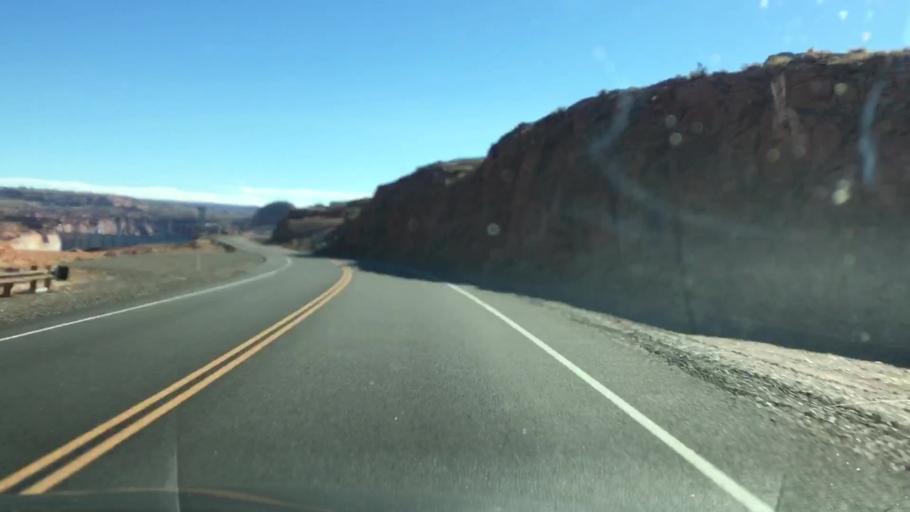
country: US
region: Arizona
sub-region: Coconino County
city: Page
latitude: 36.9586
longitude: -111.4933
